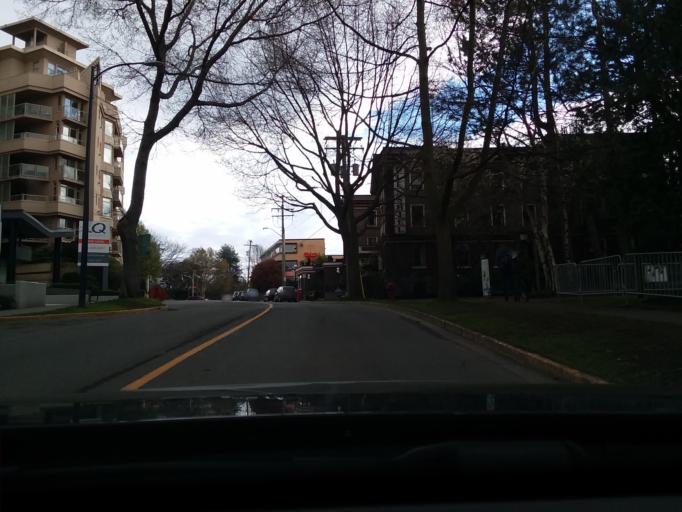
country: CA
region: British Columbia
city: Victoria
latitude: 48.4198
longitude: -123.3663
